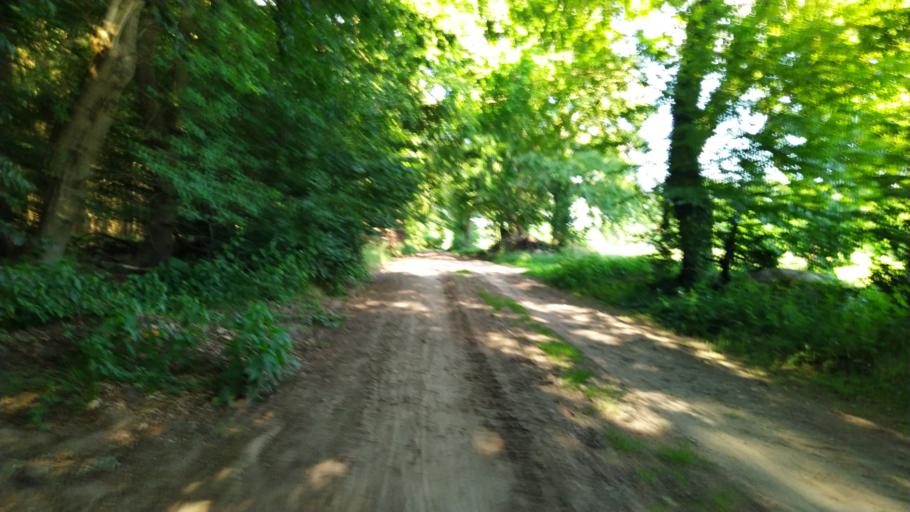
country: DE
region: Lower Saxony
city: Lintig
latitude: 53.5977
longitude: 8.9138
